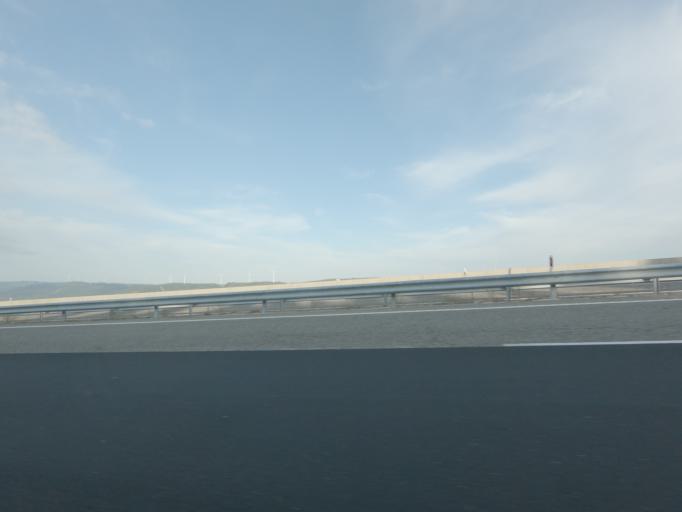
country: PT
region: Vila Real
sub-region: Vila Pouca de Aguiar
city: Vila Pouca de Aguiar
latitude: 41.5215
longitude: -7.6446
